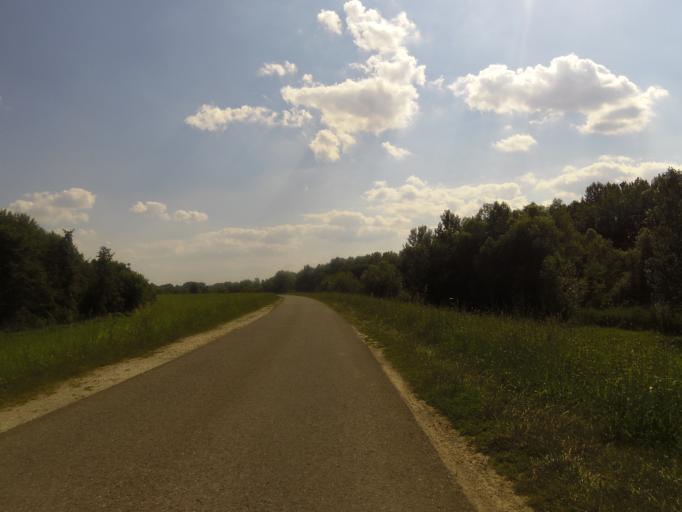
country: HU
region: Jasz-Nagykun-Szolnok
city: Tiszaszolos
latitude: 47.6026
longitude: 20.7092
